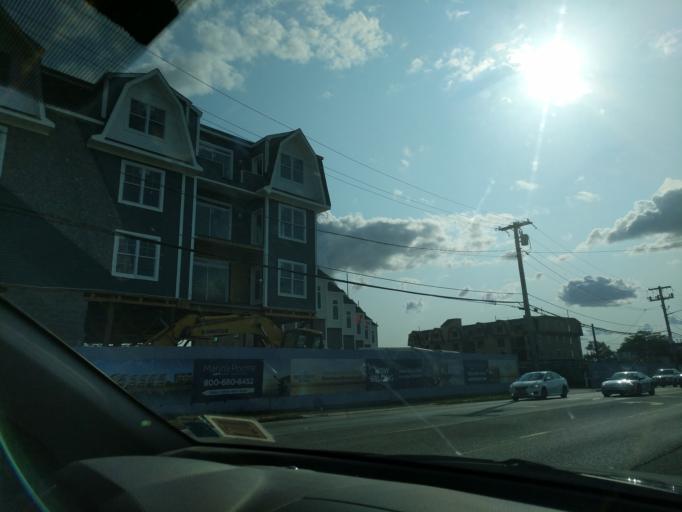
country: US
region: New York
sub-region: Nassau County
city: East Rockaway
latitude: 40.6409
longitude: -73.6576
